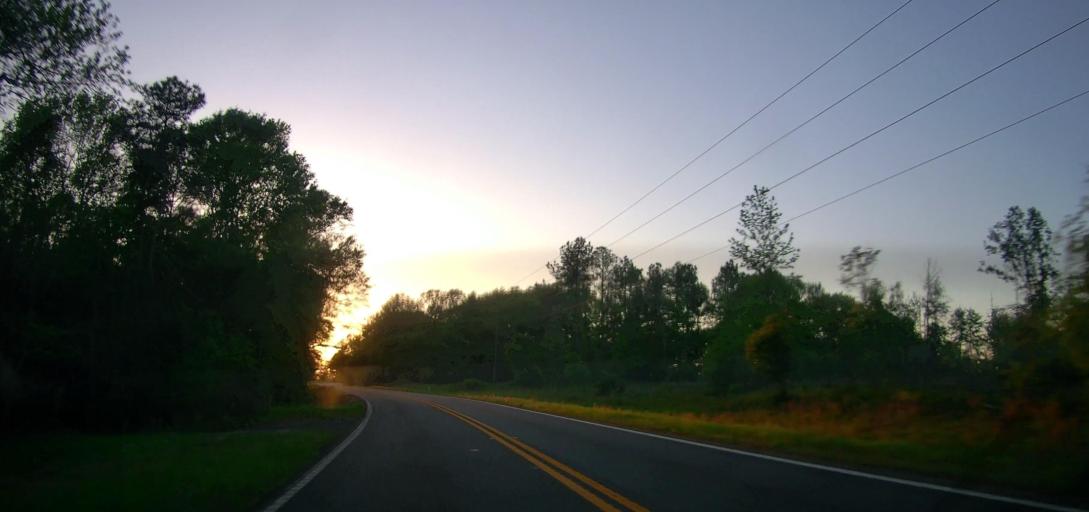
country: US
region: Georgia
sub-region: Marion County
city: Buena Vista
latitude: 32.3696
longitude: -84.5451
